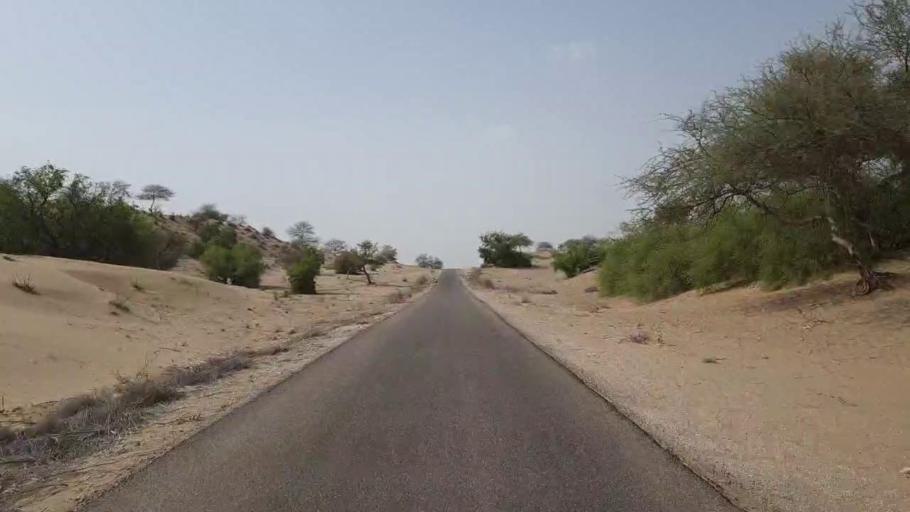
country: PK
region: Sindh
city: Mithi
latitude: 24.5871
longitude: 69.9228
